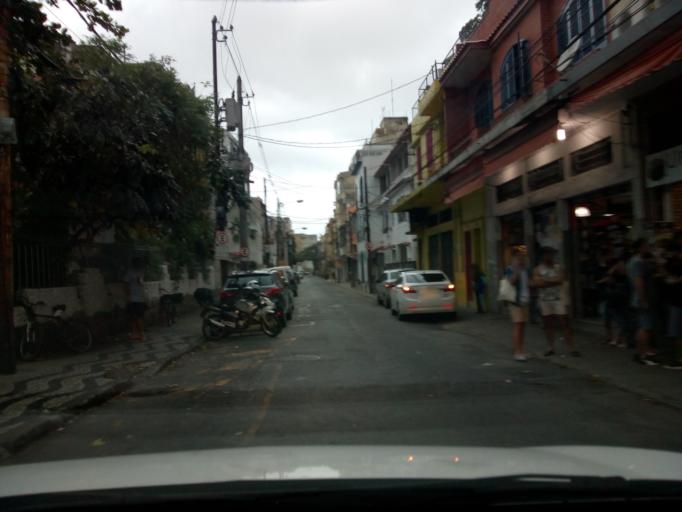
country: BR
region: Rio de Janeiro
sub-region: Rio De Janeiro
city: Rio de Janeiro
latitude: -22.9508
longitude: -43.1677
